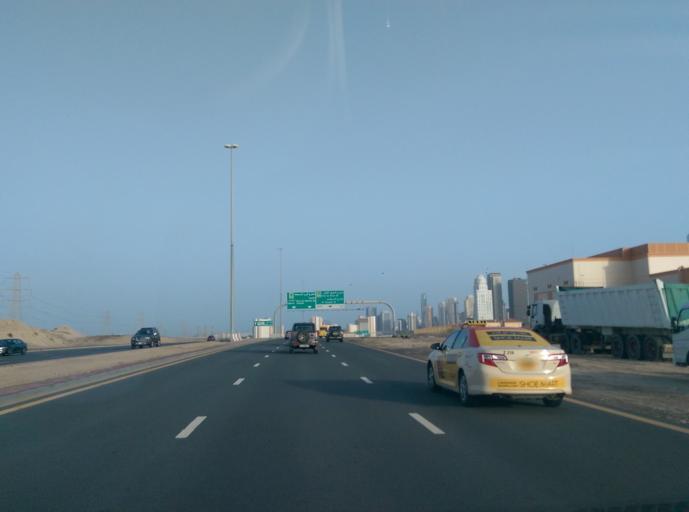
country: AE
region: Dubai
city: Dubai
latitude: 25.0488
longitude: 55.1462
